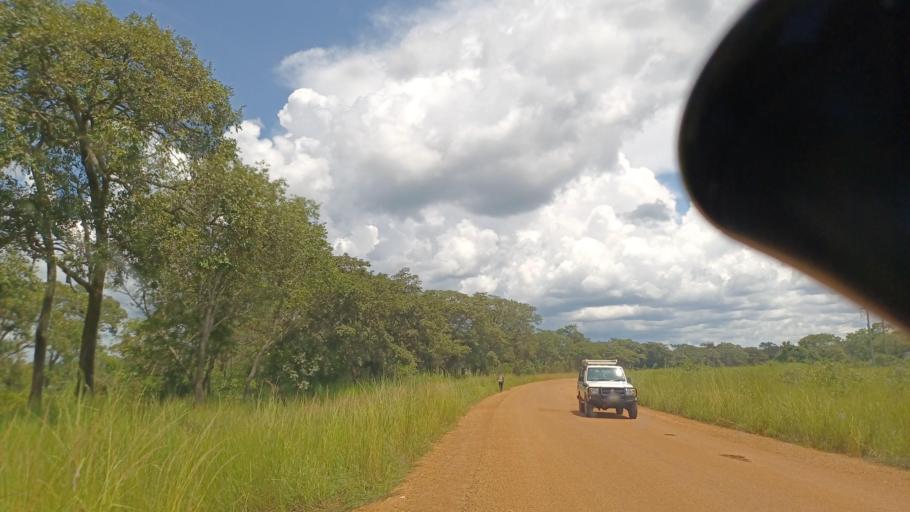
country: ZM
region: North-Western
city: Solwezi
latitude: -12.6946
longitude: 26.0401
